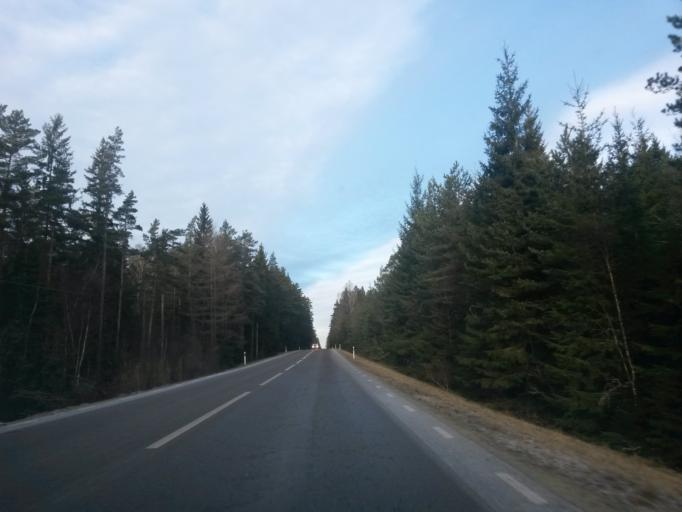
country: SE
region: Vaestra Goetaland
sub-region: Boras Kommun
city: Boras
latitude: 57.8691
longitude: 12.9311
